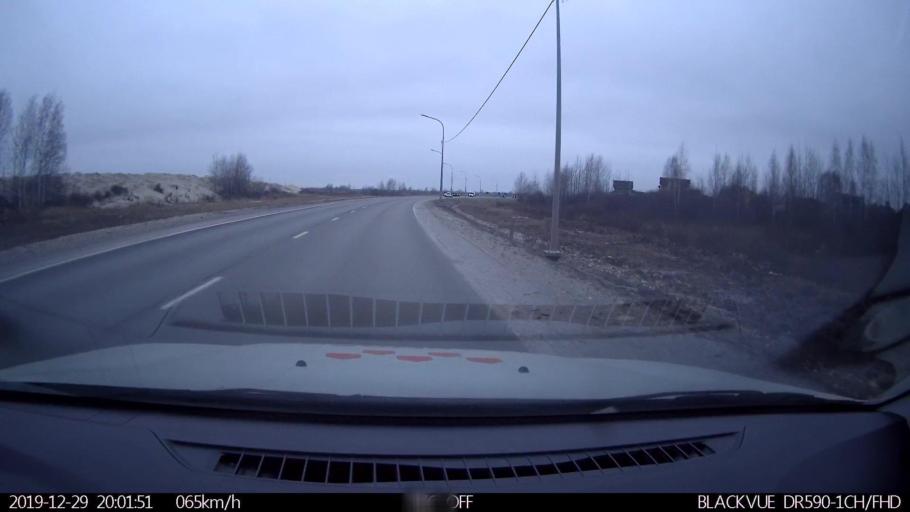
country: RU
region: Nizjnij Novgorod
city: Bor
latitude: 56.3608
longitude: 44.0372
